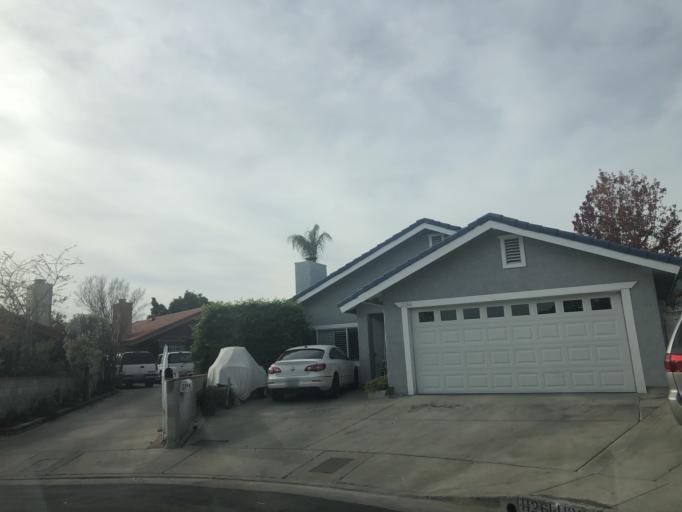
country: US
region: California
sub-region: Los Angeles County
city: San Fernando
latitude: 34.2743
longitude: -118.4341
